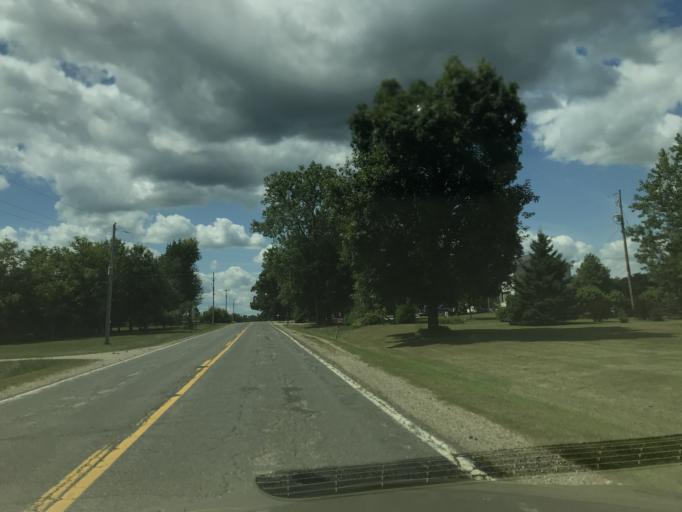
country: US
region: Michigan
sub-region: Ingham County
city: Leslie
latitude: 42.4511
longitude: -84.5514
